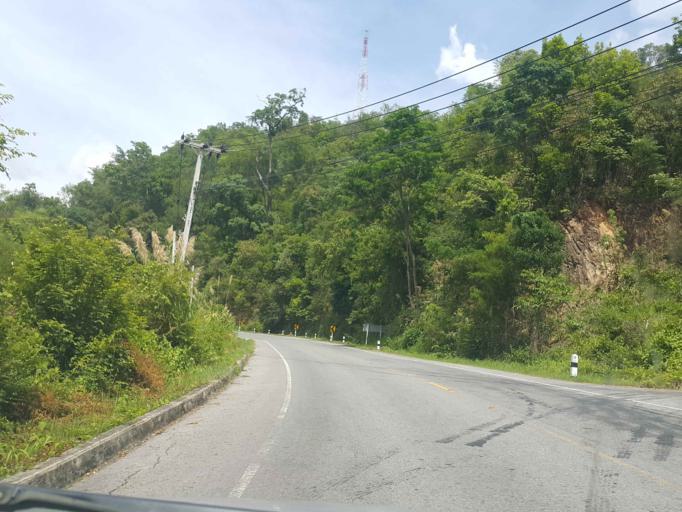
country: TH
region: Nan
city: Ban Luang
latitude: 18.8731
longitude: 100.4939
